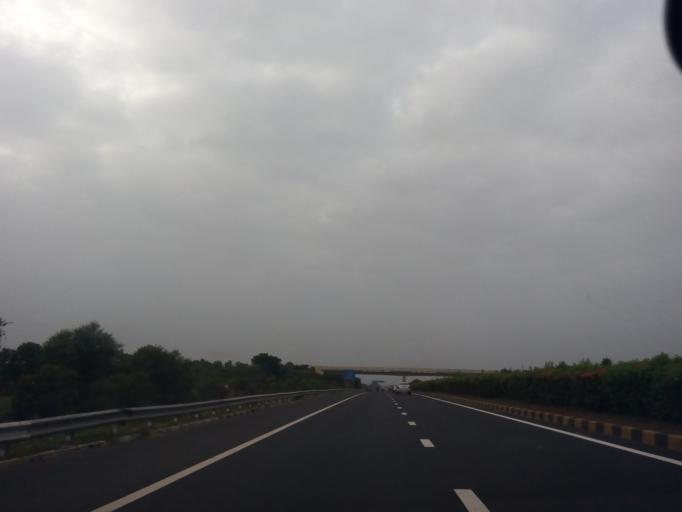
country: IN
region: Gujarat
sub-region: Kheda
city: Chaklasi
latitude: 22.6094
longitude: 72.9694
